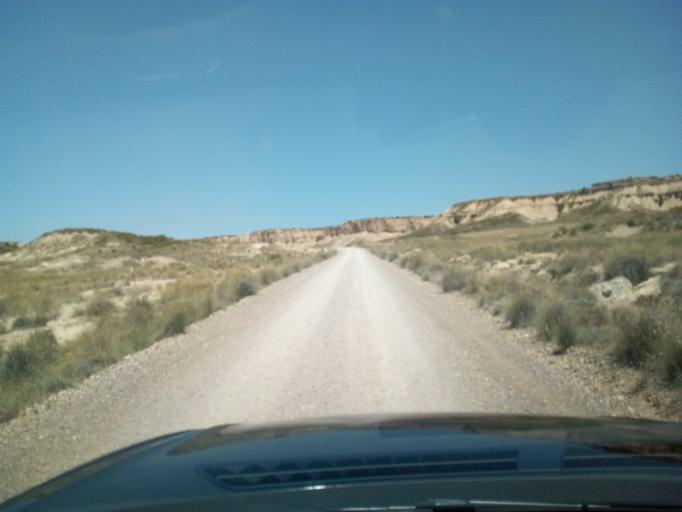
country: ES
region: Aragon
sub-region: Provincia de Zaragoza
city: Sadaba
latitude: 42.1891
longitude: -1.4118
